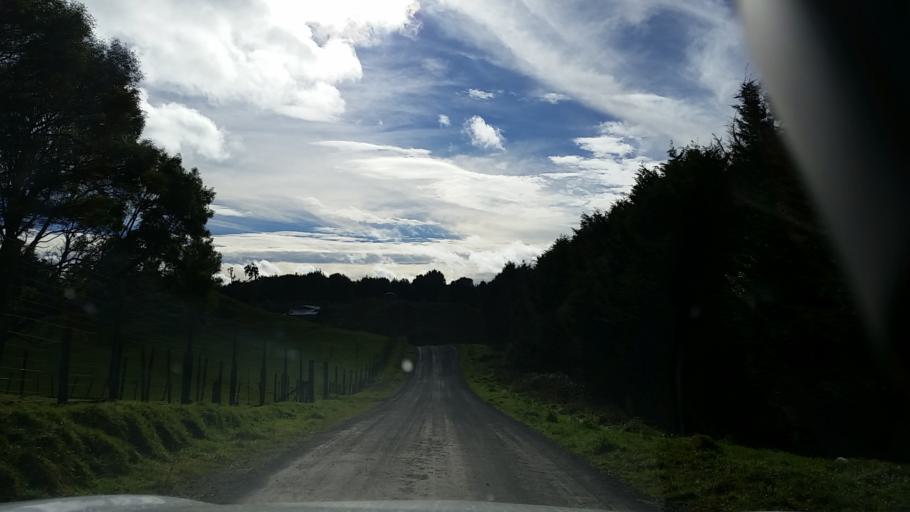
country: NZ
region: Bay of Plenty
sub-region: Rotorua District
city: Rotorua
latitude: -38.0950
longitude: 176.1038
